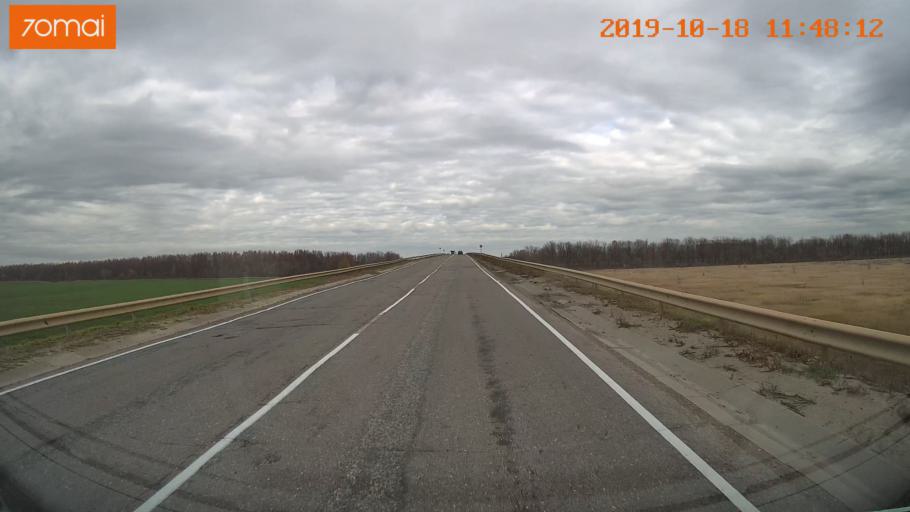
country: RU
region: Rjazan
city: Mikhaylov
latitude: 54.2371
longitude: 38.9816
